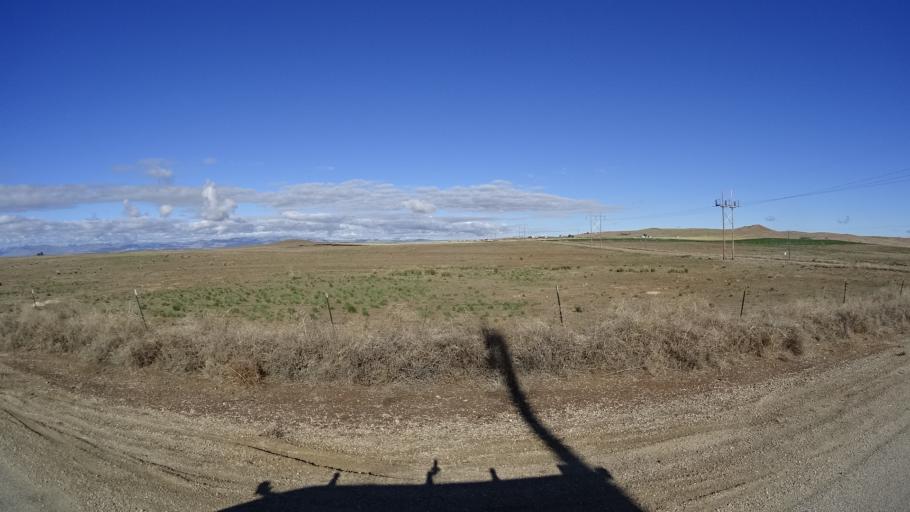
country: US
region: Idaho
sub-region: Ada County
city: Kuna
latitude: 43.4217
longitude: -116.4140
